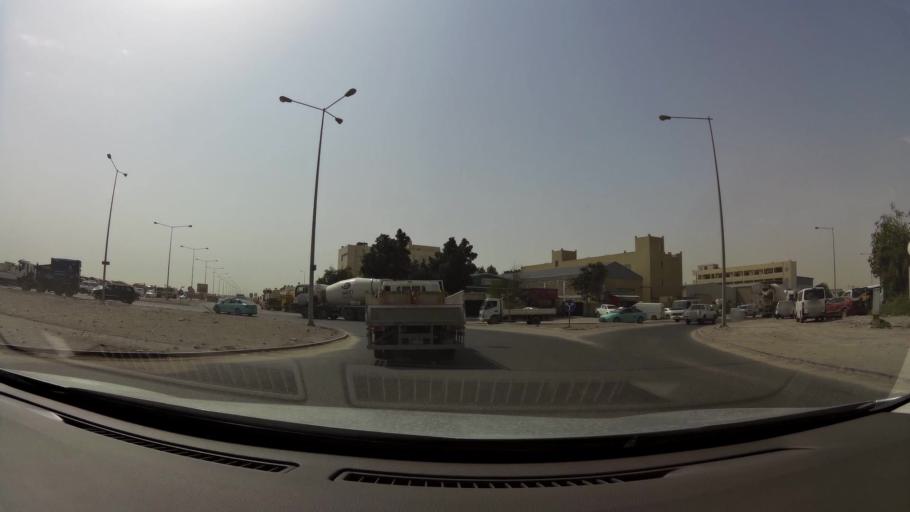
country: QA
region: Al Wakrah
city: Al Wukayr
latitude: 25.1784
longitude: 51.4652
